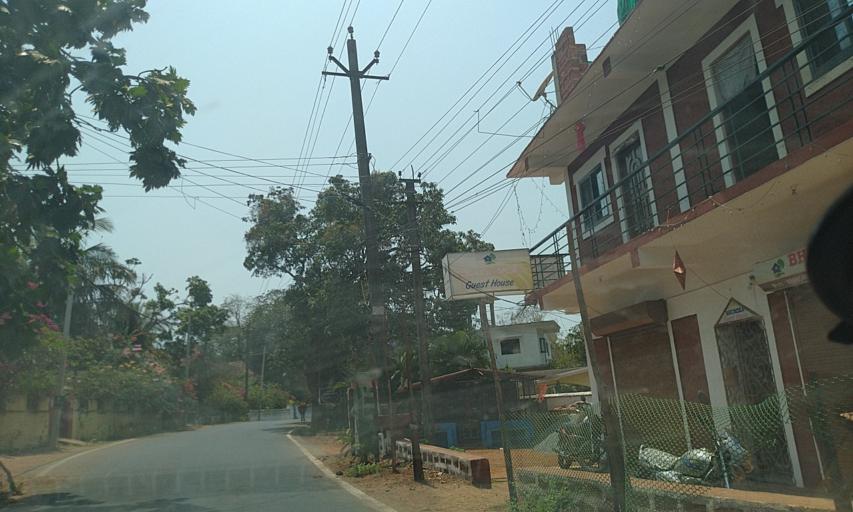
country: IN
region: Goa
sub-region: North Goa
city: Solim
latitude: 15.5956
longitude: 73.7788
